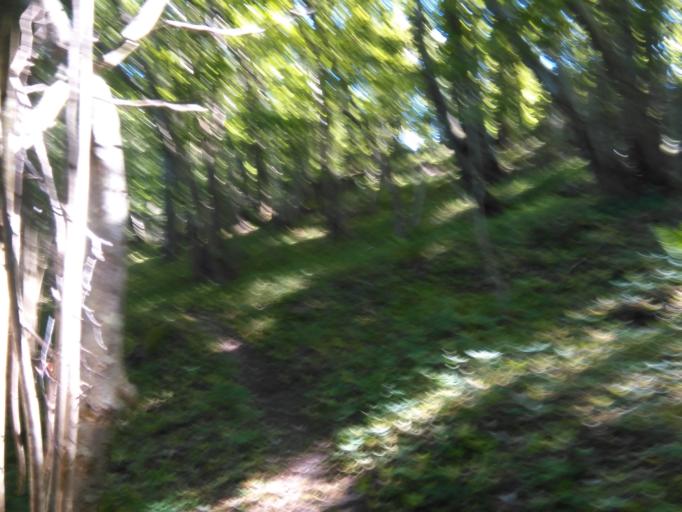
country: DK
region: Capital Region
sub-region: Bornholm Kommune
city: Ronne
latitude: 55.2572
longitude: 14.7704
